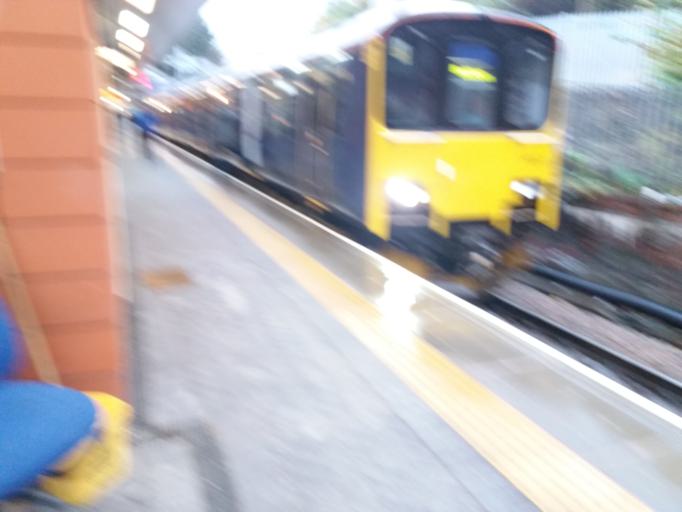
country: GB
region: England
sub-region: City and Borough of Salford
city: Salford
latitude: 53.4869
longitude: -2.2757
